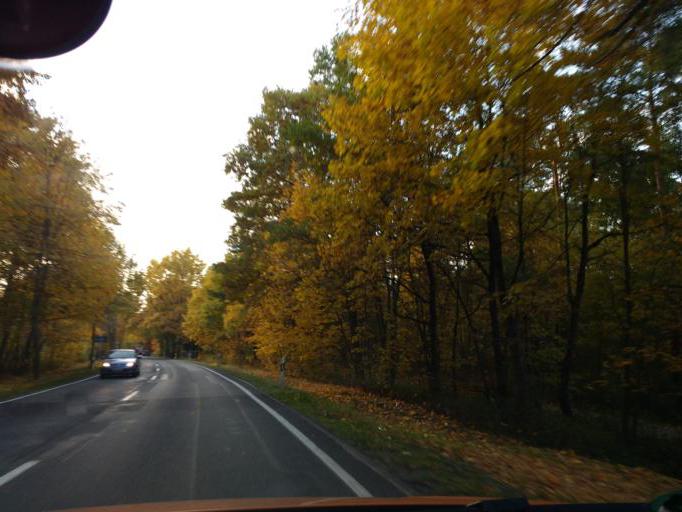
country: DE
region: Brandenburg
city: Grunheide
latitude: 52.4256
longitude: 13.8069
